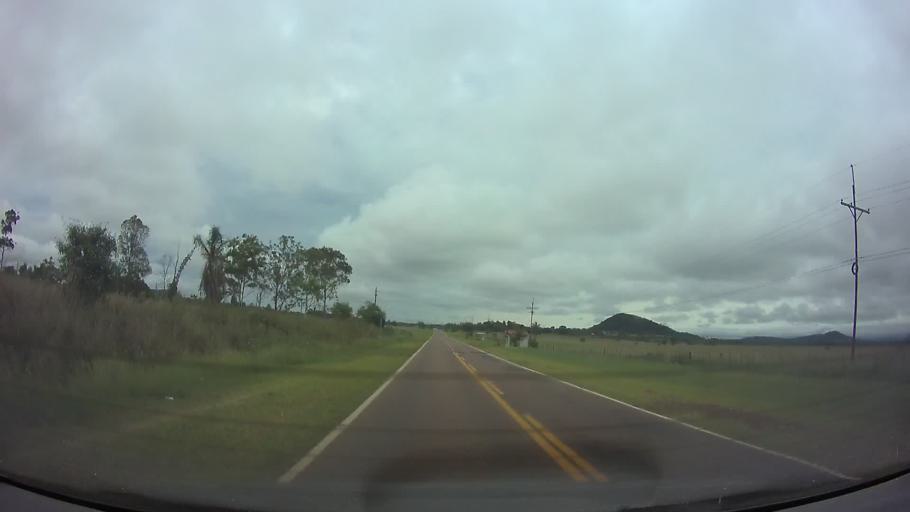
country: PY
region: Paraguari
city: Carapegua
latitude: -25.8154
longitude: -57.1760
